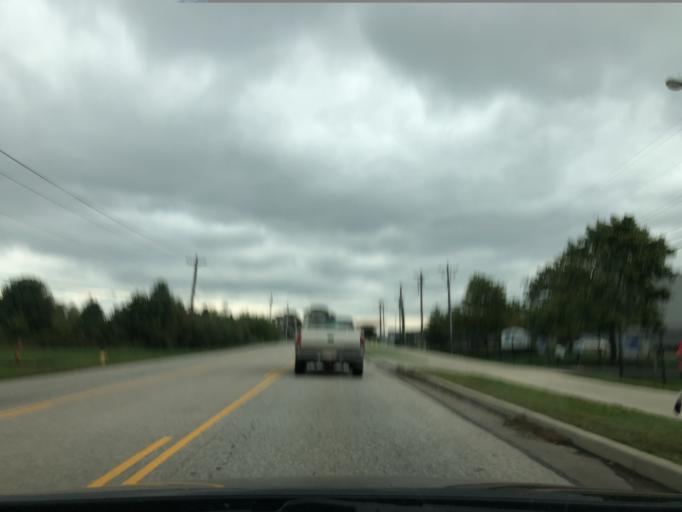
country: US
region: Kentucky
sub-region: Campbell County
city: Fort Thomas
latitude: 39.1072
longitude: -84.4248
